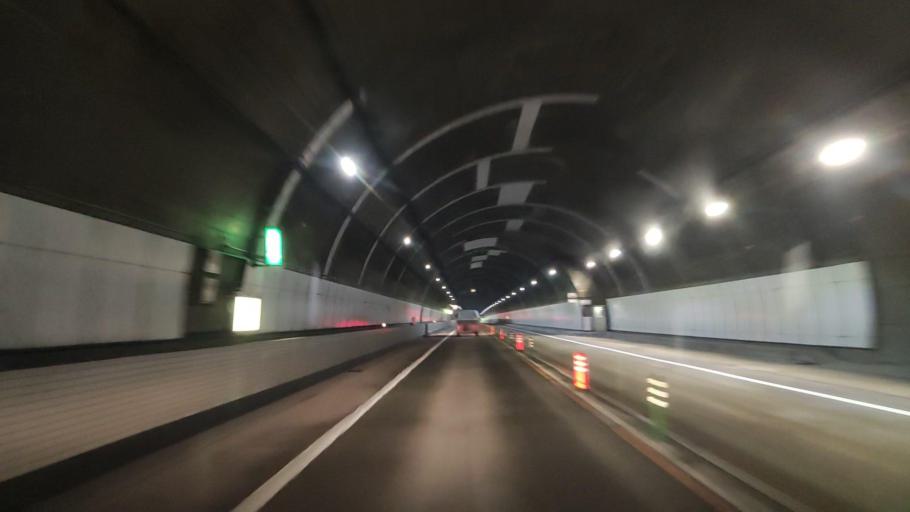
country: JP
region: Nagano
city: Hotaka
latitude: 36.1971
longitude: 137.5895
